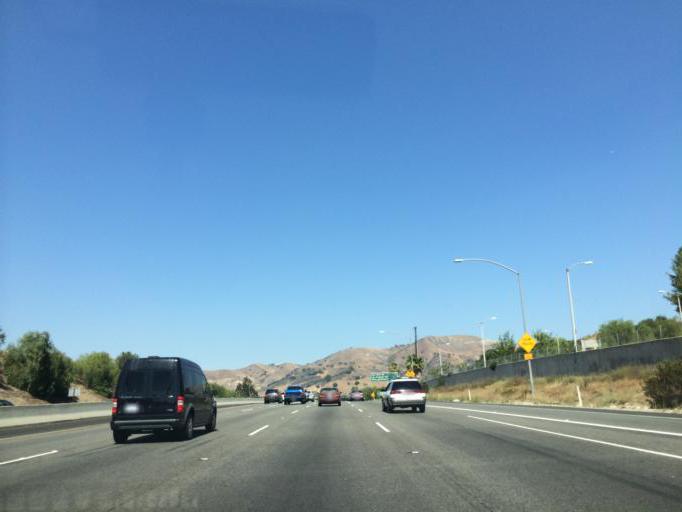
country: US
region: California
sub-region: Los Angeles County
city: Agoura
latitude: 34.1386
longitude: -118.7201
